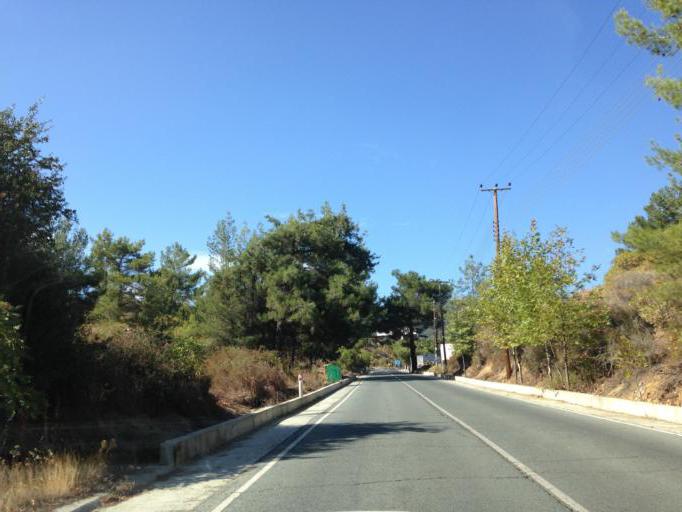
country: CY
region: Limassol
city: Pachna
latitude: 34.8855
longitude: 32.8399
